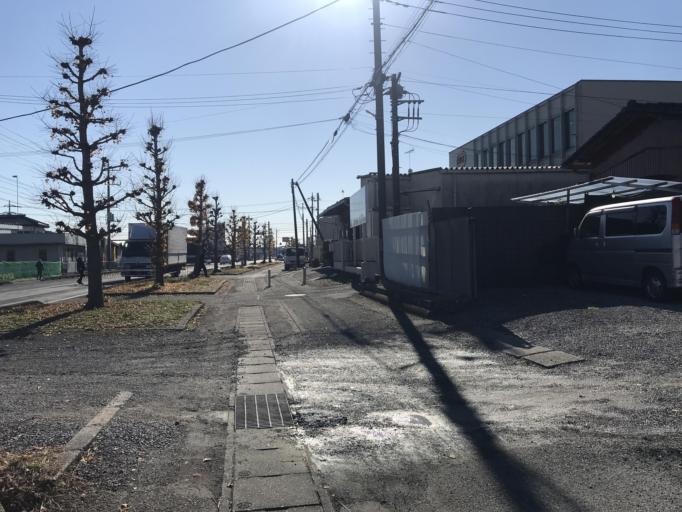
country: JP
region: Ibaraki
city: Sakai
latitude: 36.1243
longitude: 139.7993
